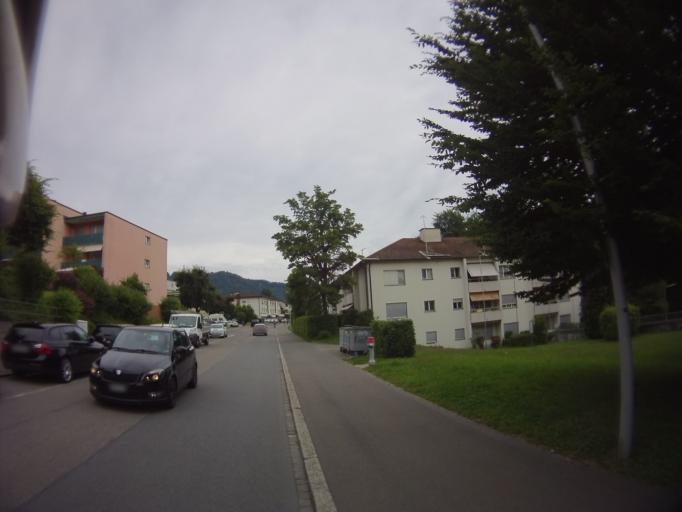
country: CH
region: Zurich
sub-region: Bezirk Horgen
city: Adliswil / Huendli-Zopf
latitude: 47.3154
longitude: 8.5185
